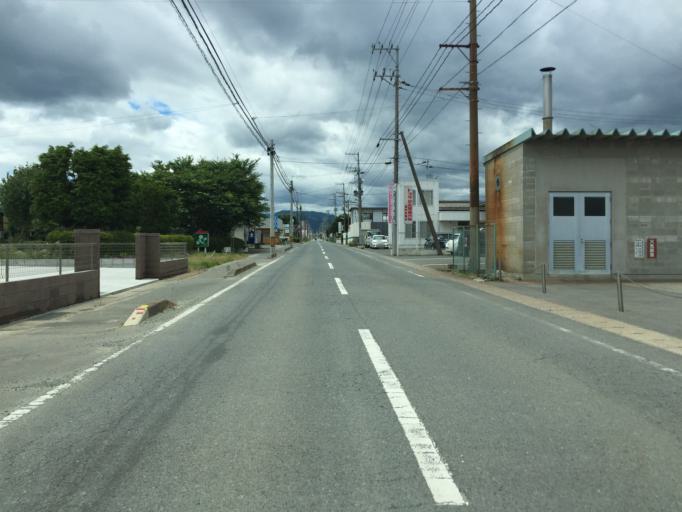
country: JP
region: Fukushima
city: Namie
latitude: 37.6375
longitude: 140.9956
